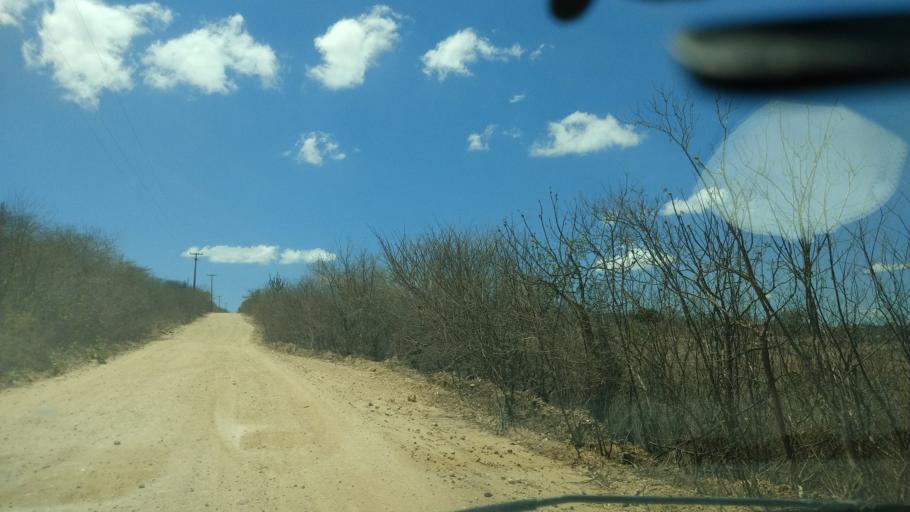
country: BR
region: Rio Grande do Norte
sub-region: Cerro Cora
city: Cerro Cora
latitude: -6.0133
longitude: -36.3265
